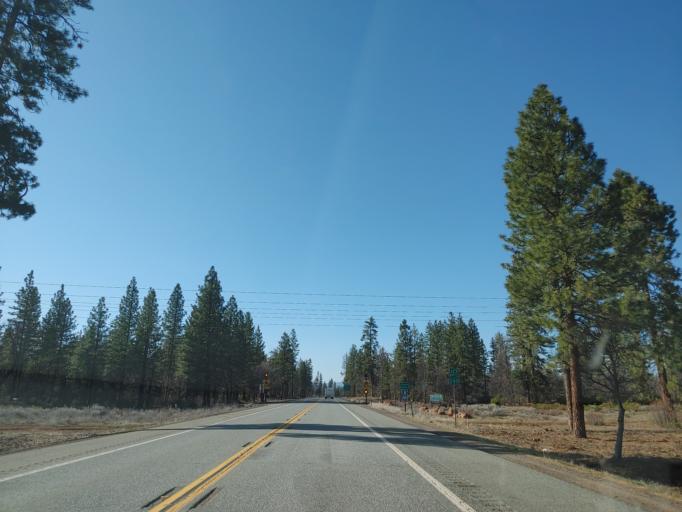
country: US
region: California
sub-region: Shasta County
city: Burney
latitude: 40.9333
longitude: -121.6037
